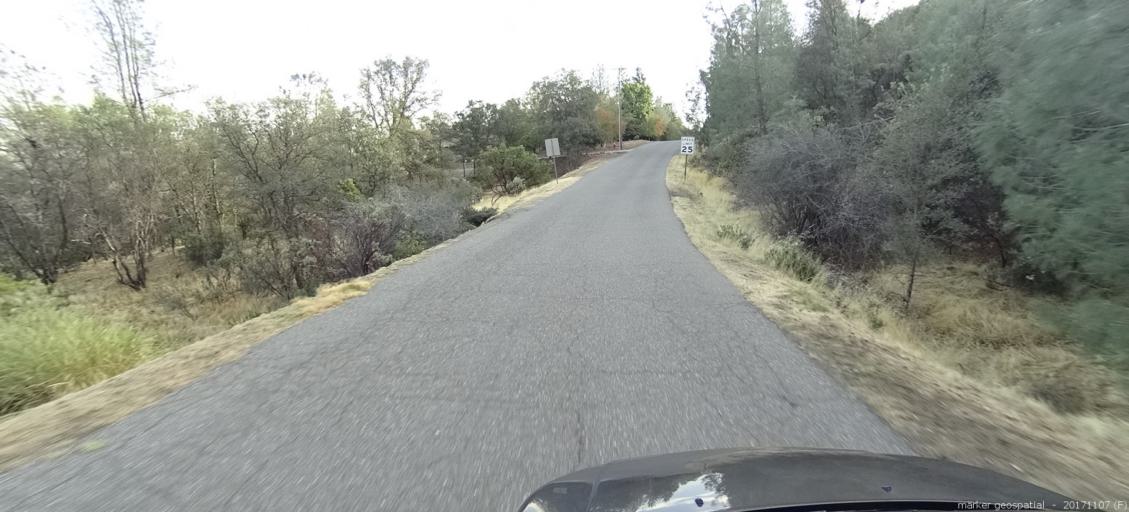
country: US
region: California
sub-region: Shasta County
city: Shasta
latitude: 40.5298
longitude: -122.4861
